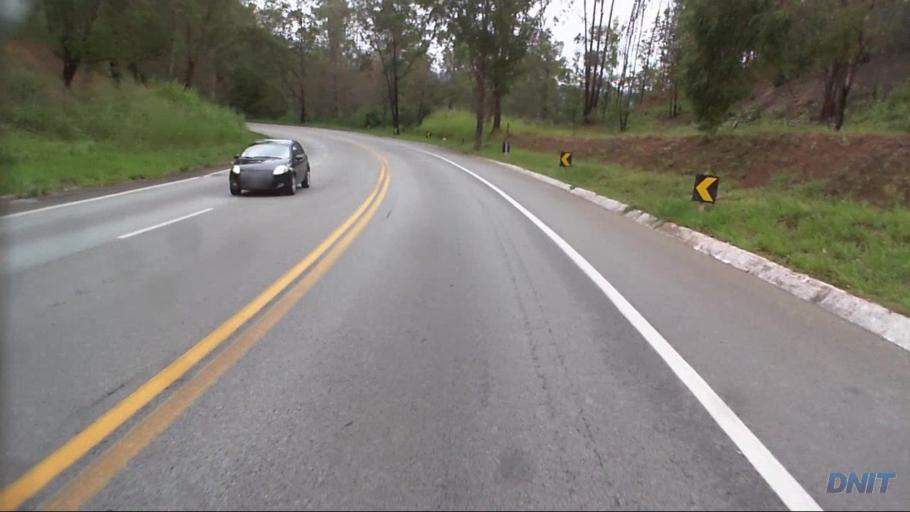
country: BR
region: Minas Gerais
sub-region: Joao Monlevade
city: Joao Monlevade
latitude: -19.8532
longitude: -43.1120
